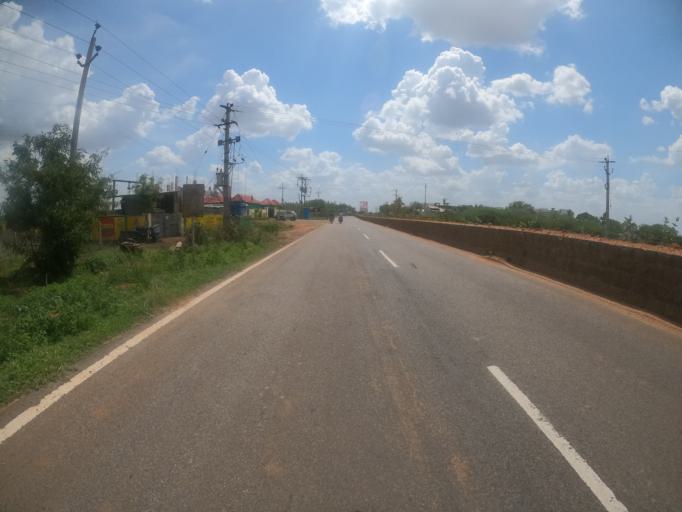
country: IN
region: Telangana
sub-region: Rangareddi
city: Sriramnagar
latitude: 17.3050
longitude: 78.1509
